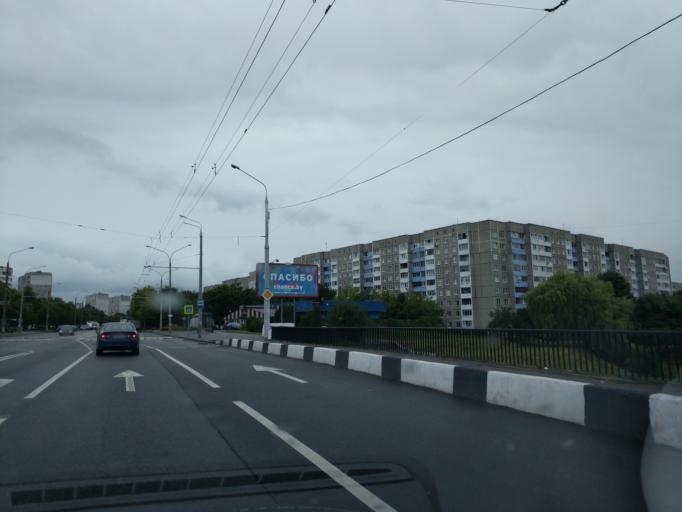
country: BY
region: Minsk
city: Novoye Medvezhino
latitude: 53.8587
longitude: 27.4711
